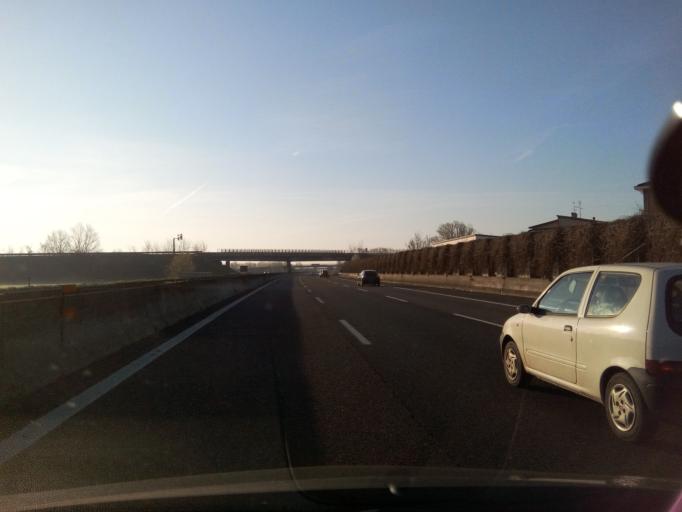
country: IT
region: Lombardy
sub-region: Provincia di Lodi
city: Guardamiglio
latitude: 45.1125
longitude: 9.6841
